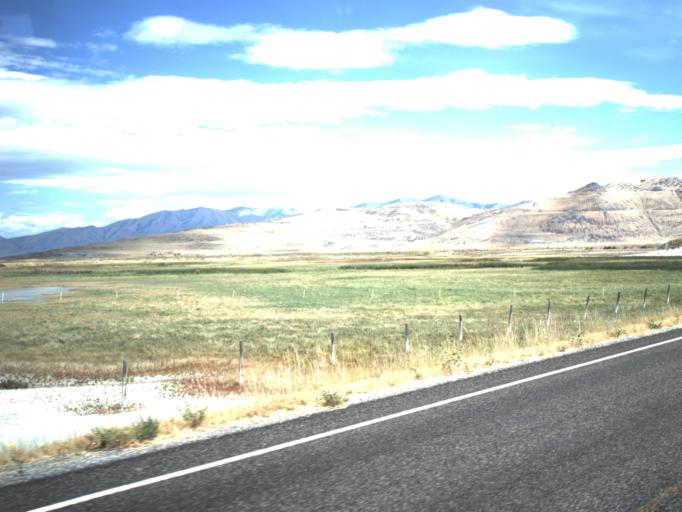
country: US
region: Utah
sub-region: Box Elder County
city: Tremonton
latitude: 41.6042
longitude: -112.3150
